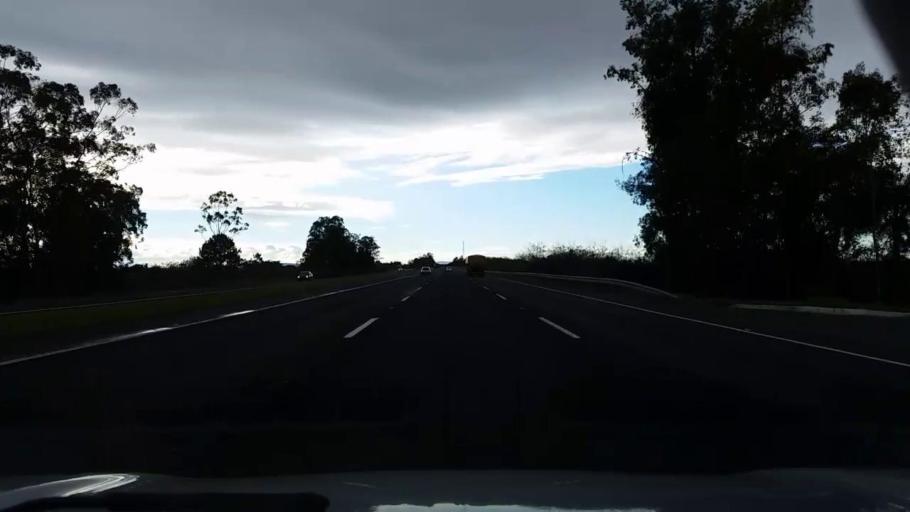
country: BR
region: Rio Grande do Sul
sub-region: Taquara
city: Taquara
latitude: -29.8898
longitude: -50.6887
